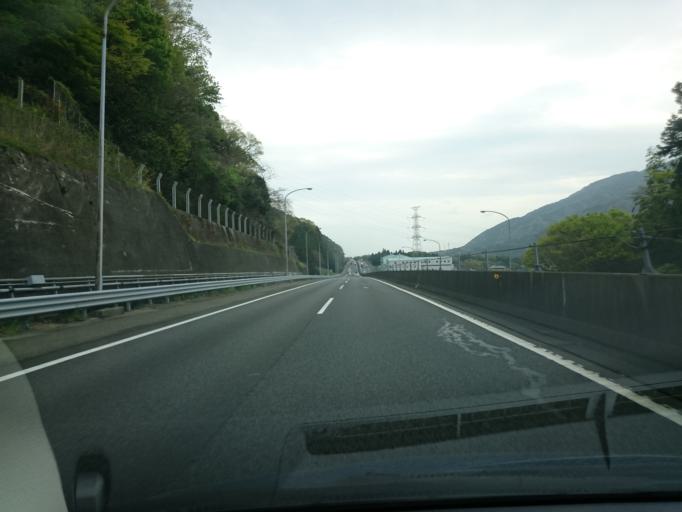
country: JP
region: Gifu
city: Tarui
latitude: 35.3425
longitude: 136.4950
